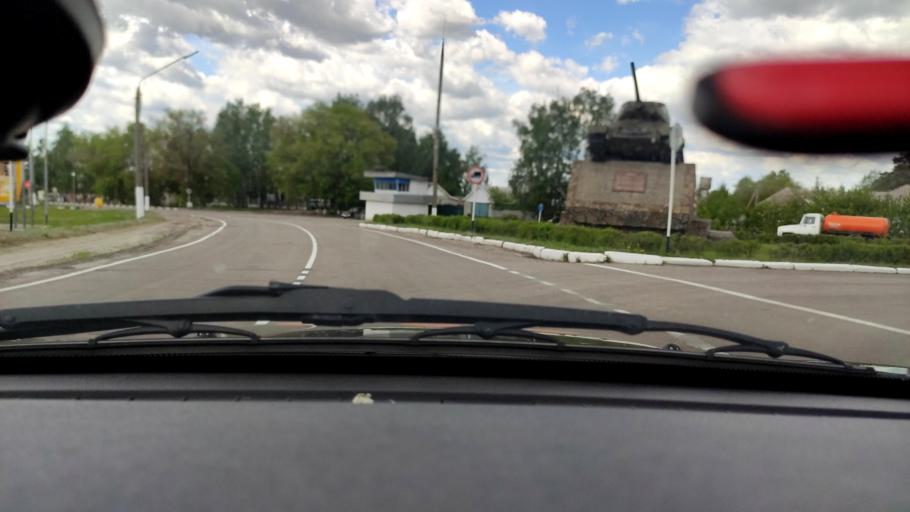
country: RU
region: Voronezj
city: Rossosh'
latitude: 51.0874
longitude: 38.6455
